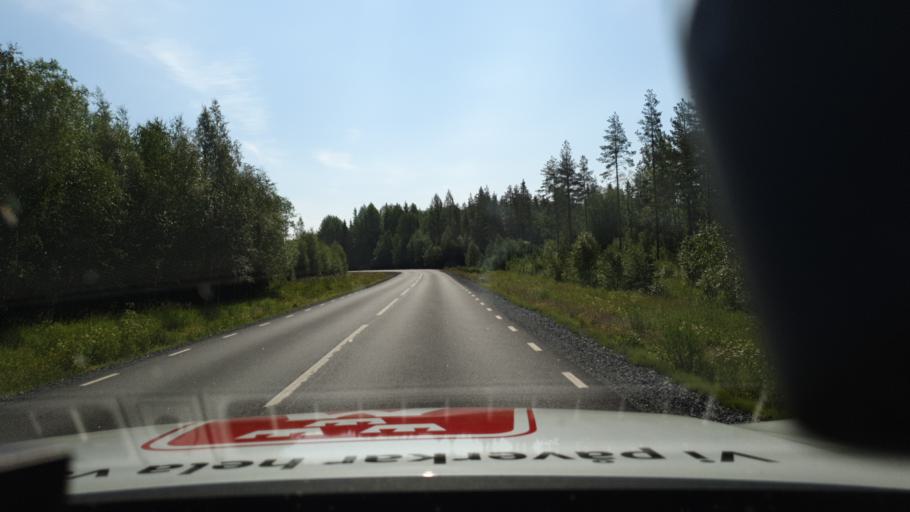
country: SE
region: Norrbotten
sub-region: Bodens Kommun
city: Saevast
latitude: 65.8424
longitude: 21.8017
